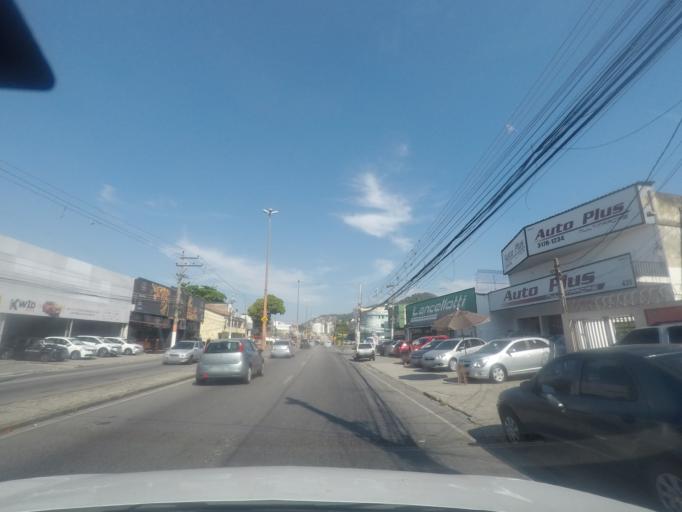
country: BR
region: Rio de Janeiro
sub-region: Sao Joao De Meriti
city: Sao Joao de Meriti
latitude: -22.8808
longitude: -43.3534
